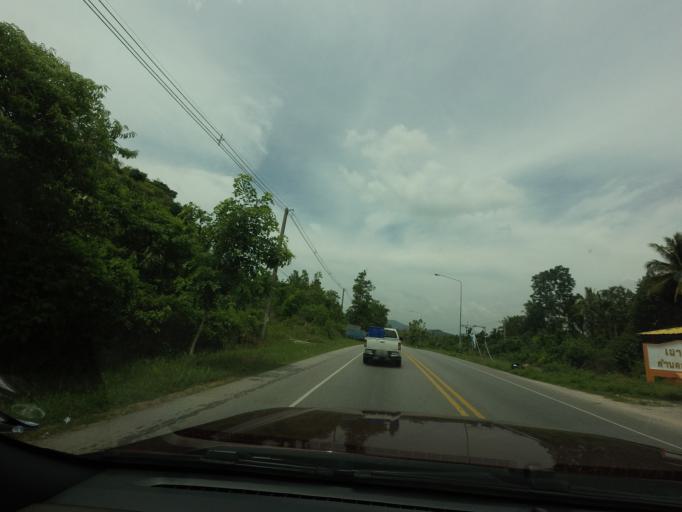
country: TH
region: Pattani
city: Mae Lan
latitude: 6.6246
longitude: 101.3044
